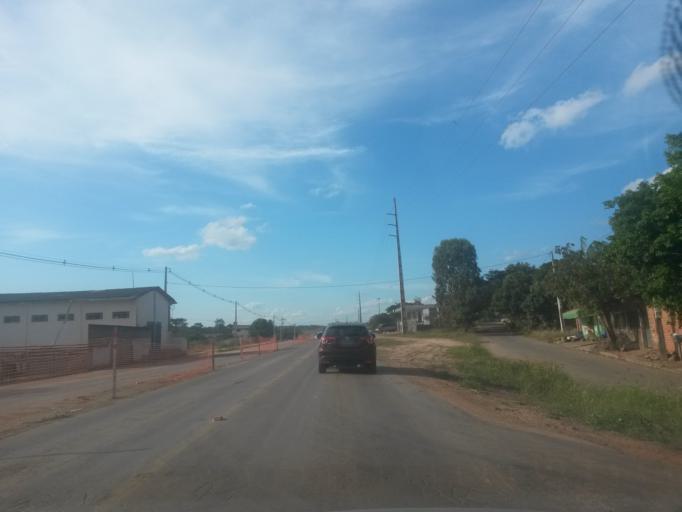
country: BR
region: Mato Grosso
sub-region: Cuiaba
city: Cuiaba
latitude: -15.5355
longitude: -56.0763
